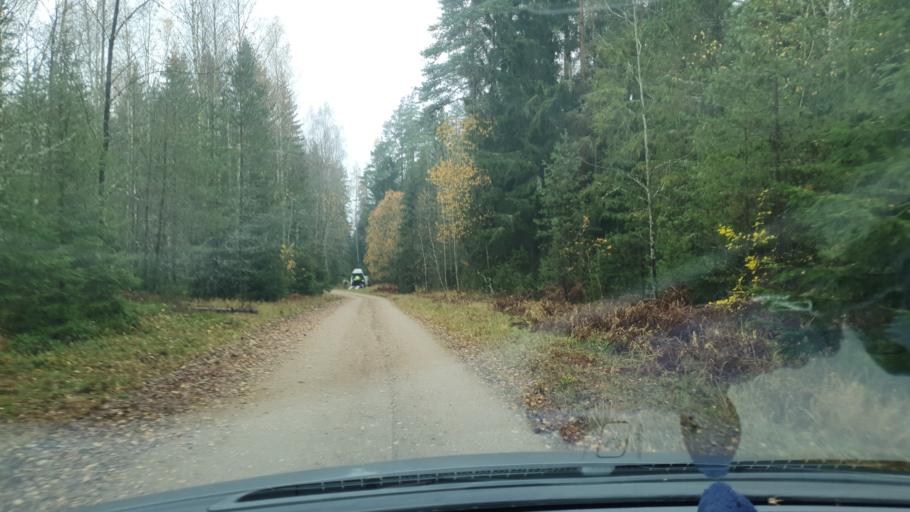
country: EE
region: Viljandimaa
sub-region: Karksi vald
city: Karksi-Nuia
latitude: 57.9733
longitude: 25.6148
